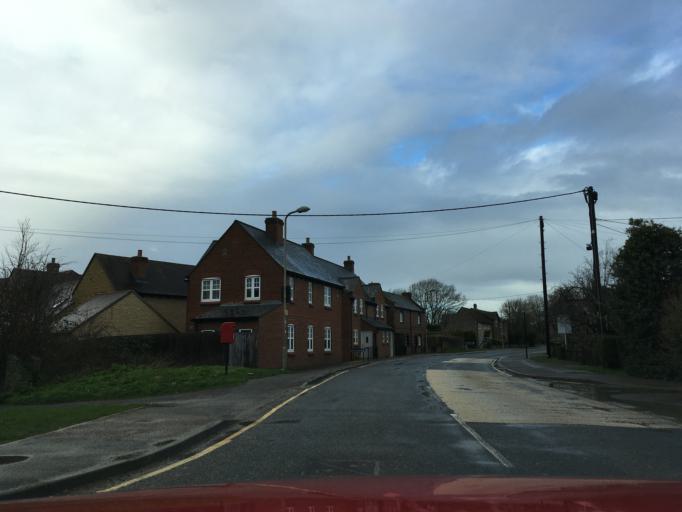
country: GB
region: England
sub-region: Oxfordshire
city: Eynsham
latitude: 51.7829
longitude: -1.3821
